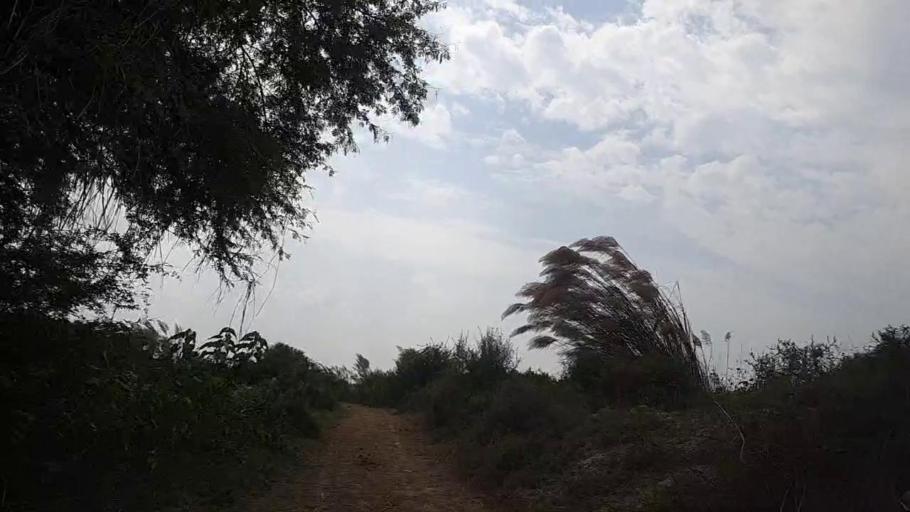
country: PK
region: Sindh
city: Mirpur Batoro
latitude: 24.6141
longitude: 68.1350
